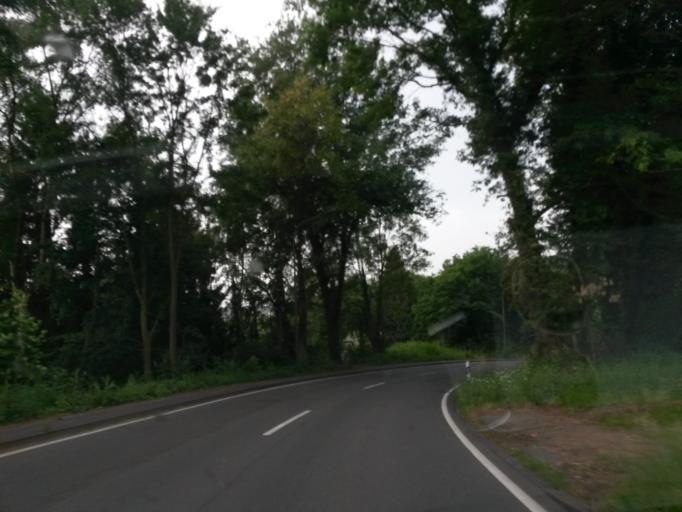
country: DE
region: North Rhine-Westphalia
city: Lohmar
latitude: 50.8567
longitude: 7.2201
